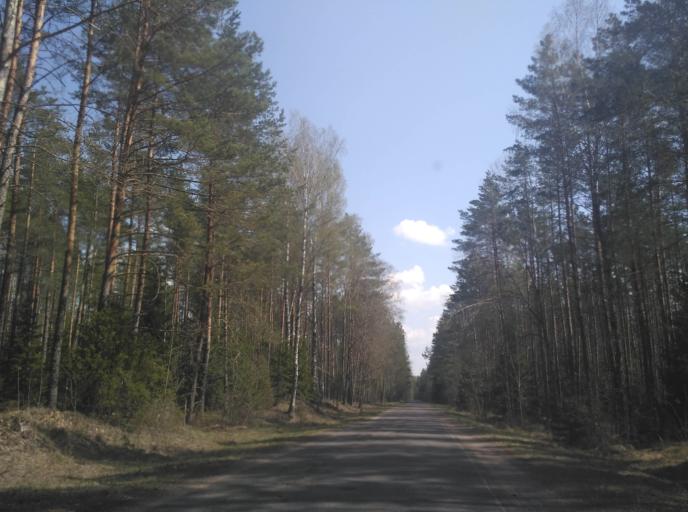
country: BY
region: Minsk
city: Loshnitsa
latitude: 54.4935
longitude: 28.6972
